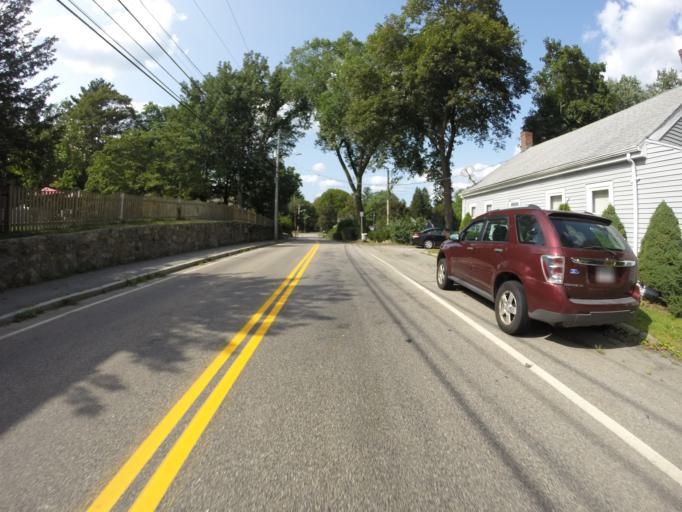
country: US
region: Massachusetts
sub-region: Bristol County
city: Easton
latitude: 42.0720
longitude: -71.1064
